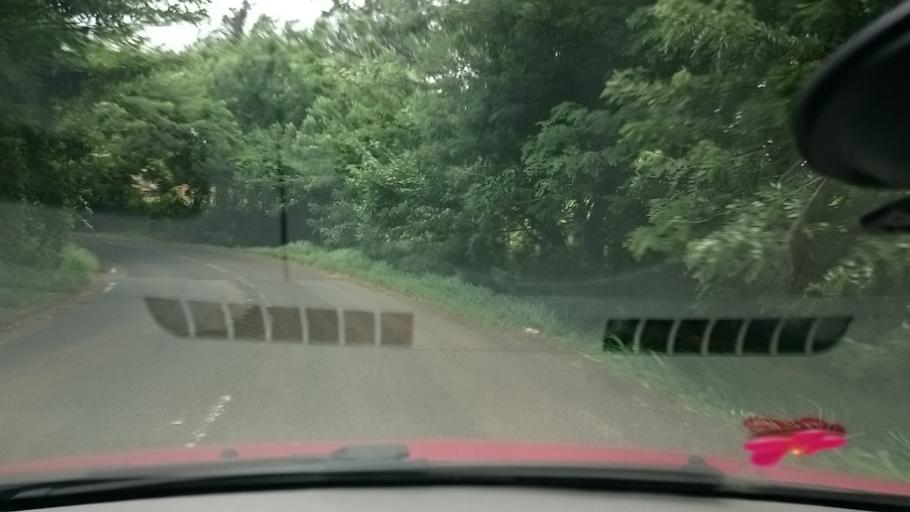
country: MQ
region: Martinique
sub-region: Martinique
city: Saint-Esprit
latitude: 14.5853
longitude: -60.9240
